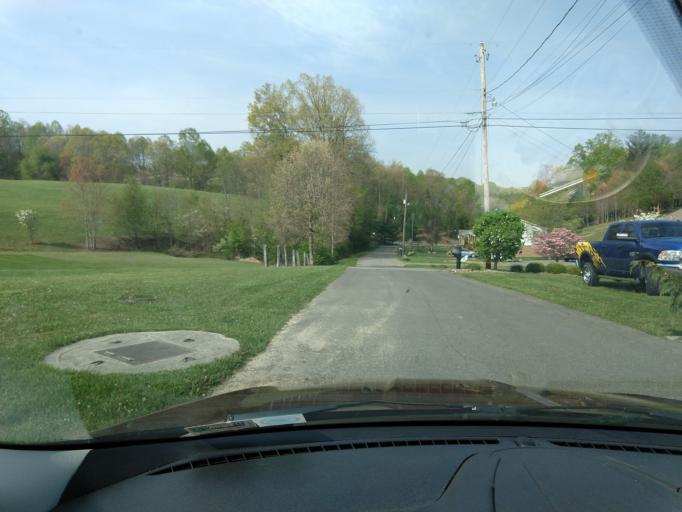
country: US
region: West Virginia
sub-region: Raleigh County
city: Crab Orchard
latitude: 37.7522
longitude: -81.2410
